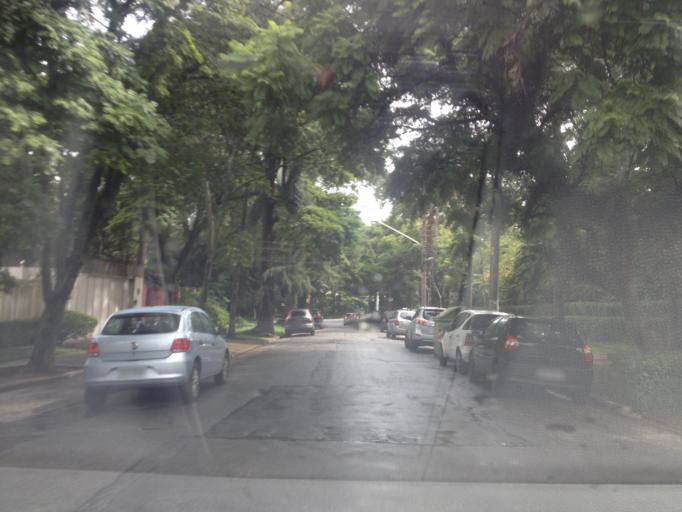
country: BR
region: Sao Paulo
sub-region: Sao Paulo
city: Sao Paulo
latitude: -23.5742
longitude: -46.6699
